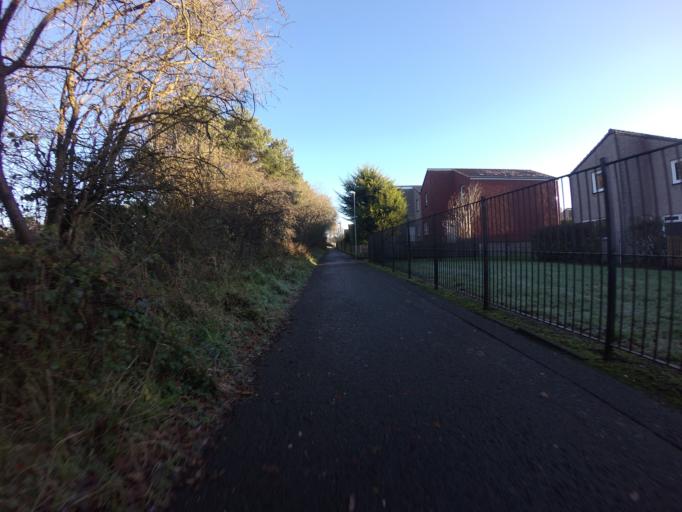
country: GB
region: Scotland
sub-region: West Lothian
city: Livingston
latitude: 55.8981
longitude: -3.5233
